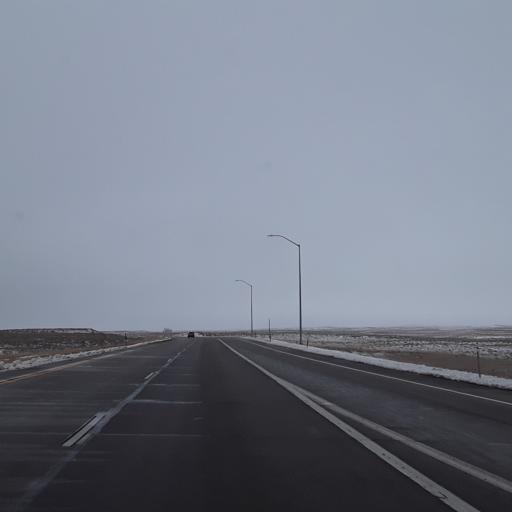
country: US
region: Colorado
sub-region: Logan County
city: Sterling
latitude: 40.6254
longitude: -103.1690
